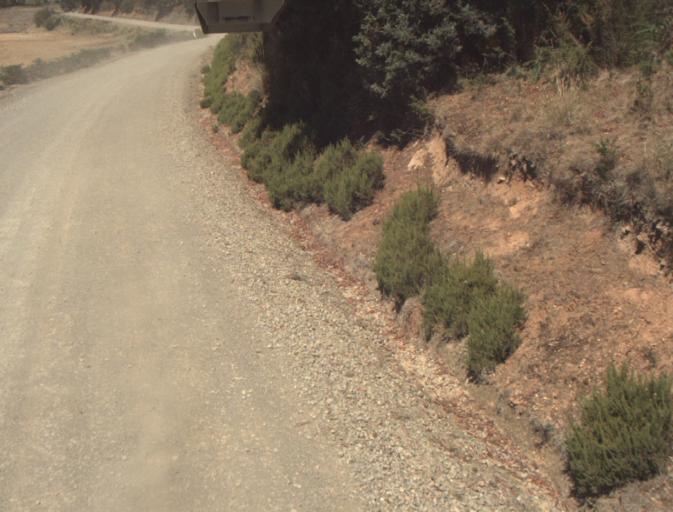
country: AU
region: Tasmania
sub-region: Dorset
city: Scottsdale
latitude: -41.3042
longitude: 147.3674
